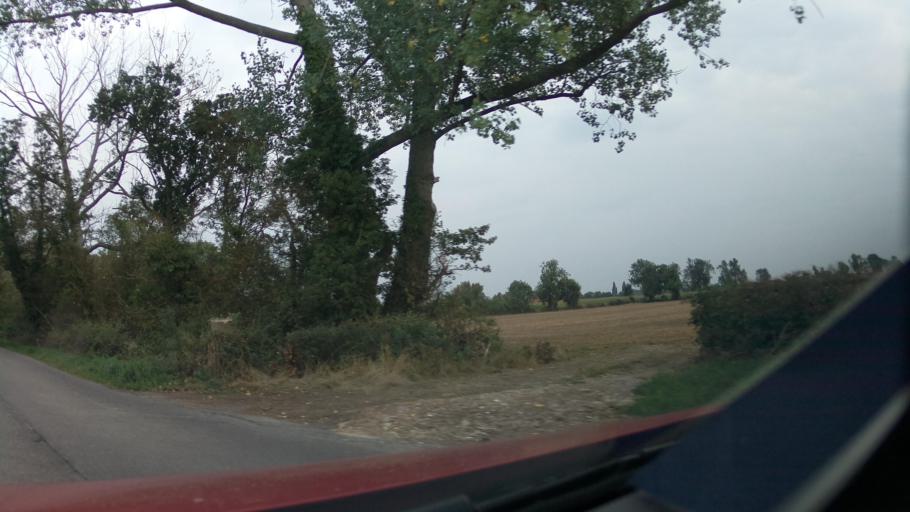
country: GB
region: England
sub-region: Lincolnshire
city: Skellingthorpe
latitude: 53.1427
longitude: -0.6494
